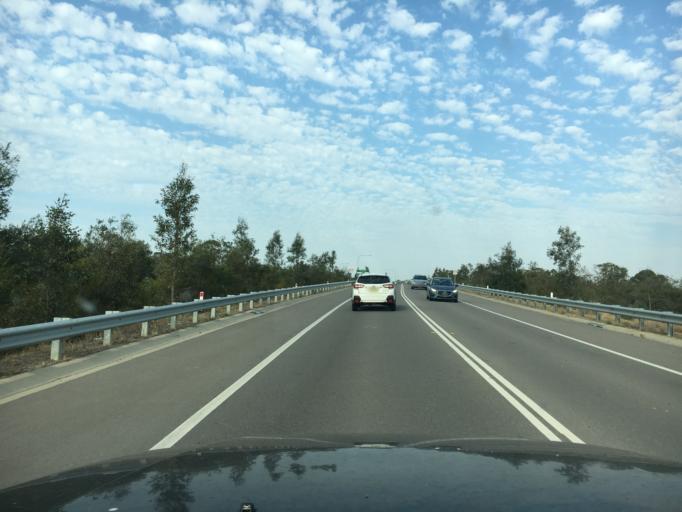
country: AU
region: New South Wales
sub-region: Cessnock
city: Branxton
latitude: -32.6657
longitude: 151.3651
